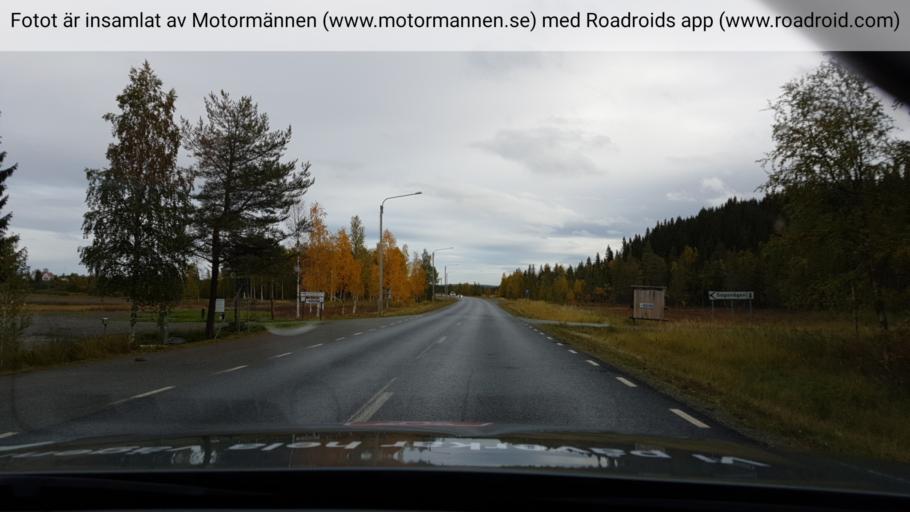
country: SE
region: Vaesterbotten
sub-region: Vilhelmina Kommun
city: Sjoberg
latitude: 64.6338
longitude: 16.3761
